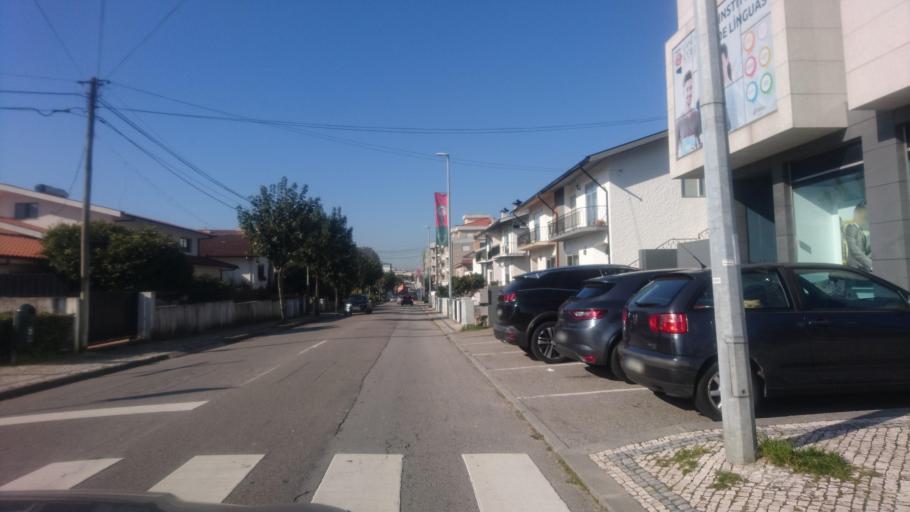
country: PT
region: Aveiro
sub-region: Santa Maria da Feira
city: Feira
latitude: 40.9259
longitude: -8.5503
